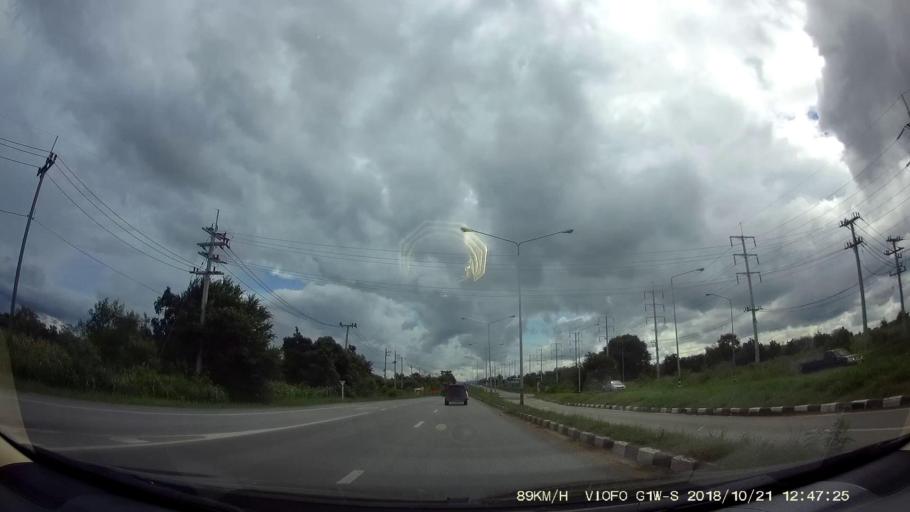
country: TH
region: Nakhon Ratchasima
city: Amphoe Sikhiu
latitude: 14.9287
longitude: 101.6839
